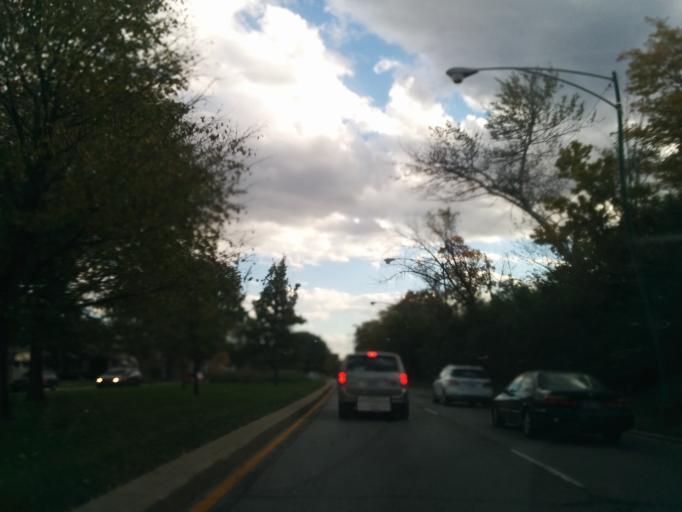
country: US
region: Illinois
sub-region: Cook County
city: Norridge
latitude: 41.9494
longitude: -87.8368
